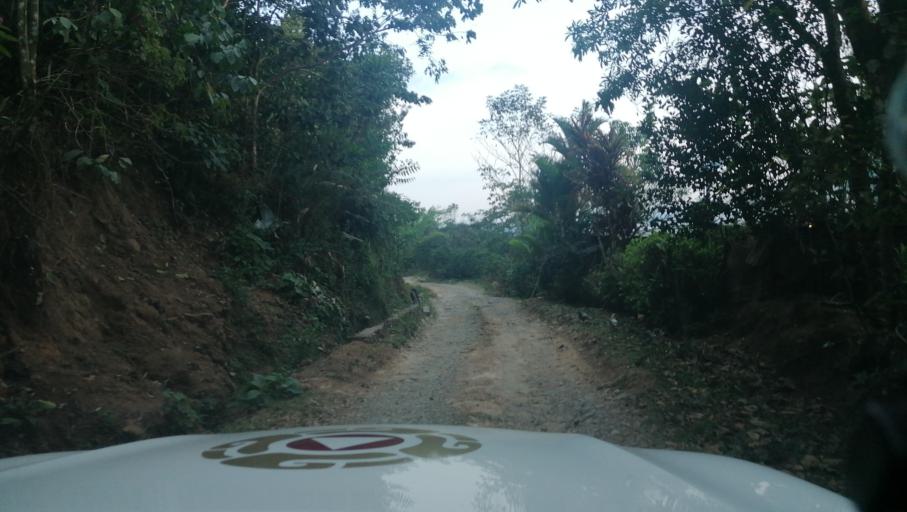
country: MX
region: Chiapas
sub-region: Cacahoatan
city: Benito Juarez
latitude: 15.0992
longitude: -92.2203
